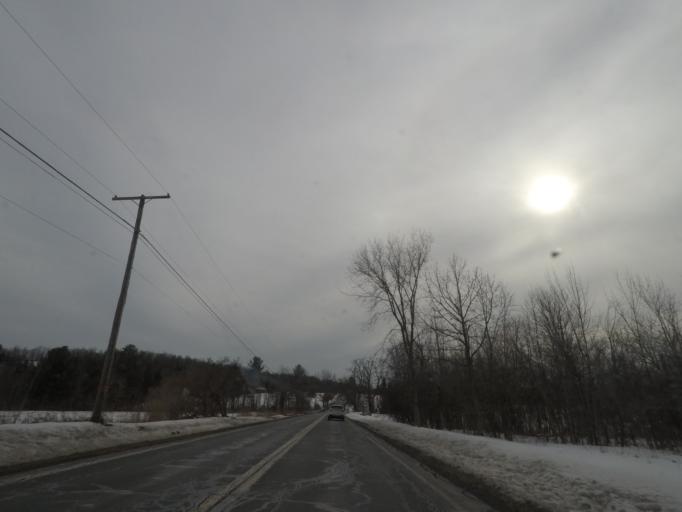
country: US
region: New York
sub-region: Albany County
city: Altamont
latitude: 42.6618
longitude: -74.1326
